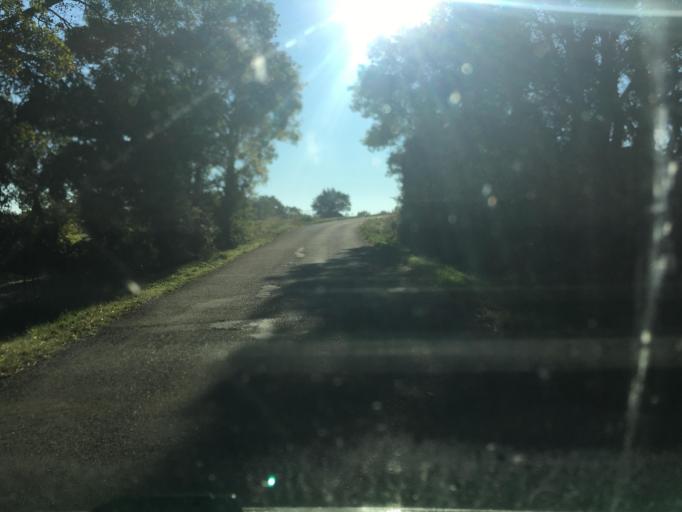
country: FR
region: Languedoc-Roussillon
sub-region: Departement du Gard
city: Barjac
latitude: 44.1801
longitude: 4.3353
